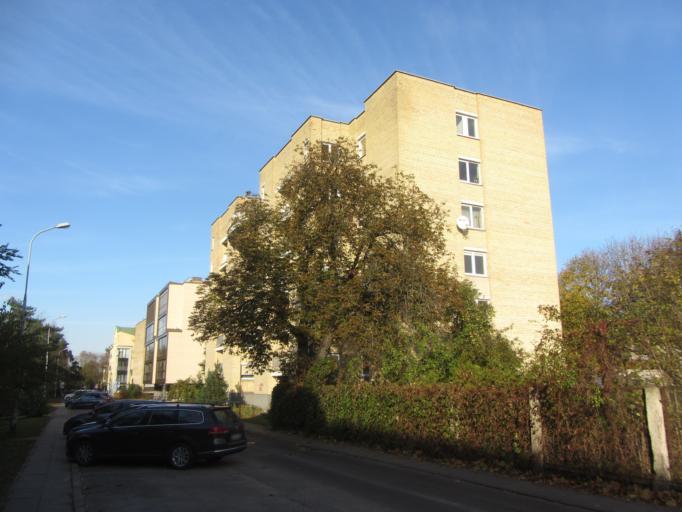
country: LT
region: Vilnius County
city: Vilkpede
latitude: 54.6804
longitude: 25.2535
